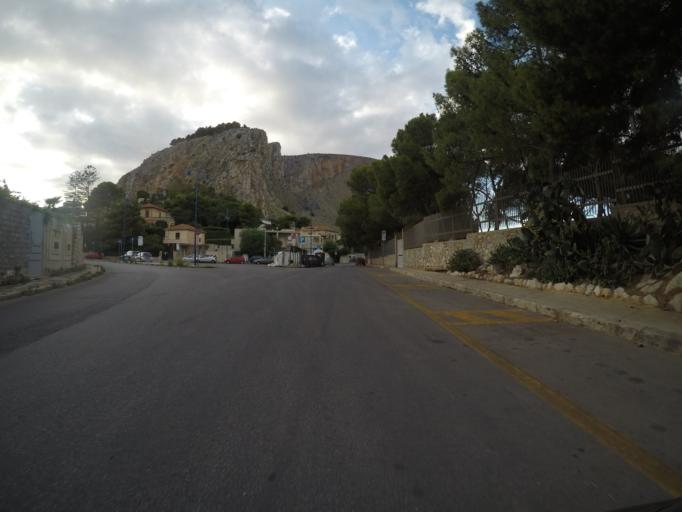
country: IT
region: Sicily
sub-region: Palermo
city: Palermo
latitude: 38.2104
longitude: 13.3284
